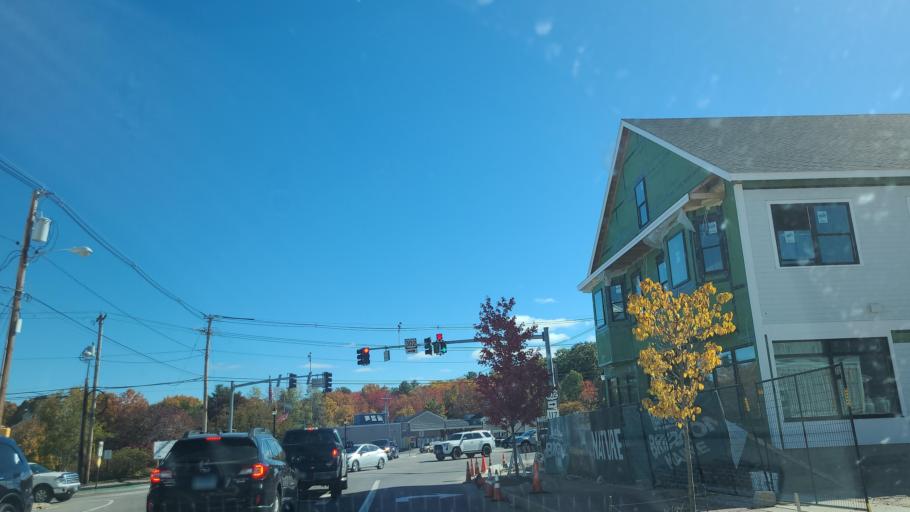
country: US
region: Maine
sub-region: Cumberland County
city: Bridgton
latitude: 44.0541
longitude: -70.7023
